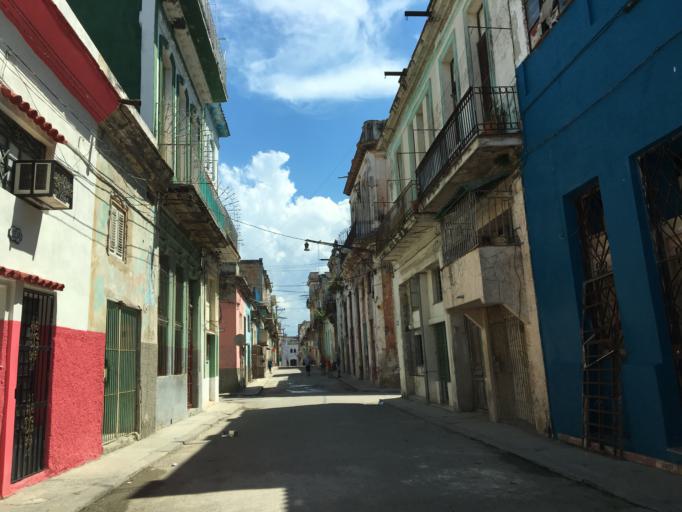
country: CU
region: La Habana
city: La Habana Vieja
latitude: 23.1287
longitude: -82.3585
